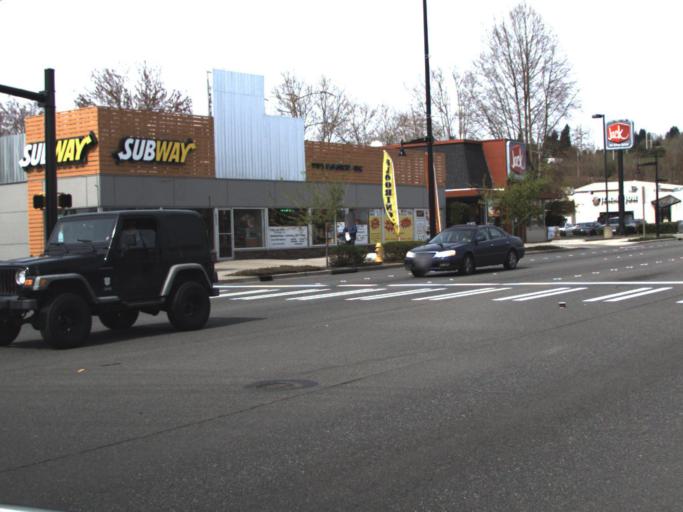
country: US
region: Washington
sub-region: King County
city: Renton
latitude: 47.4767
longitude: -122.2153
